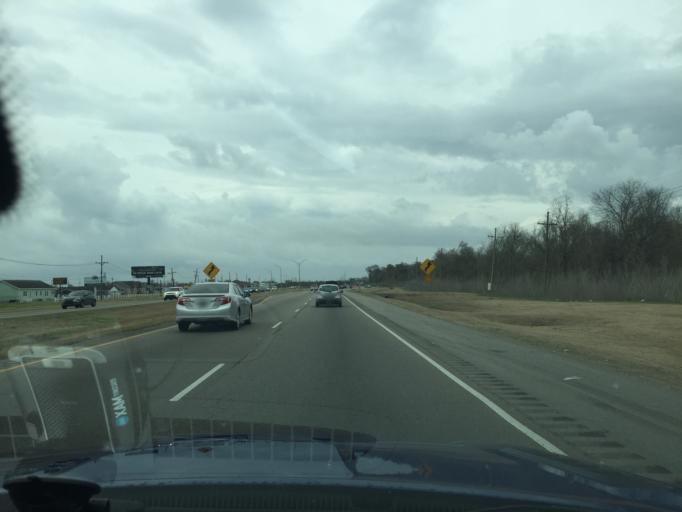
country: US
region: Louisiana
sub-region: Jefferson Parish
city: Westwego
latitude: 29.9068
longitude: -90.1604
